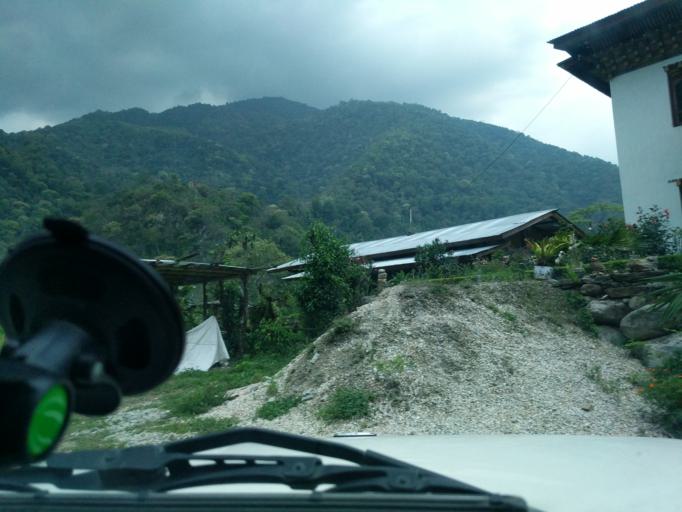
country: BT
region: Mongar
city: Mongar
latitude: 27.2756
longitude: 91.1469
